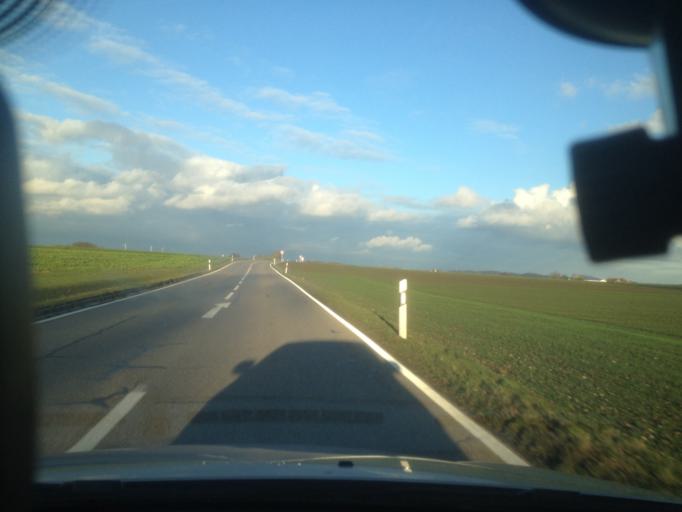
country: DE
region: Bavaria
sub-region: Swabia
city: Brunnen
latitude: 48.2453
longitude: 10.9616
